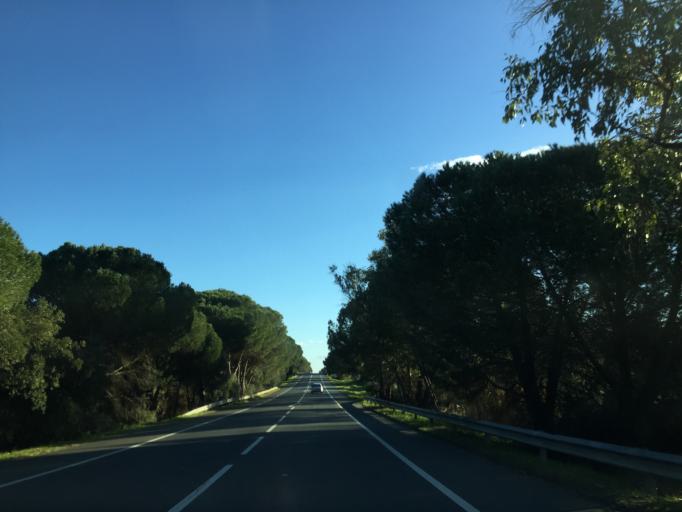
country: PT
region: Setubal
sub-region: Grandola
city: Grandola
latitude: 38.0889
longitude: -8.4180
